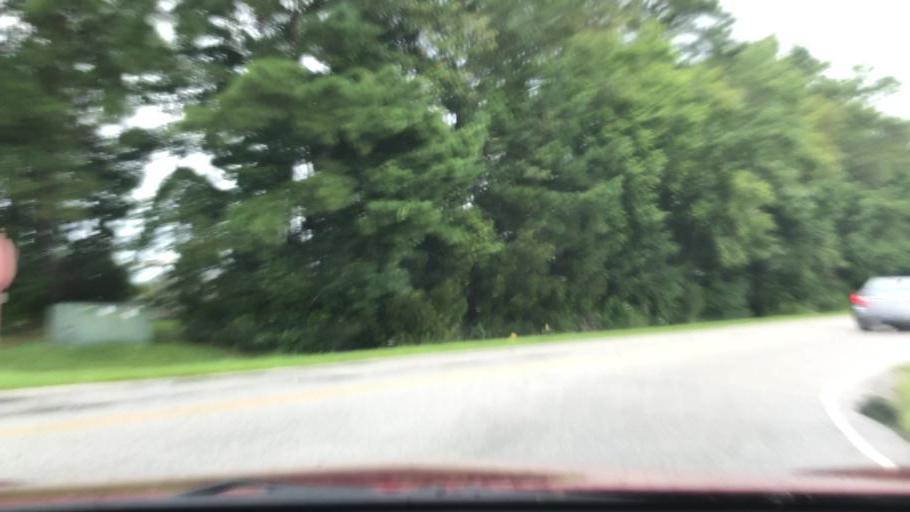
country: US
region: South Carolina
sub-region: Berkeley County
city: Hanahan
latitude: 32.8805
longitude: -80.0409
